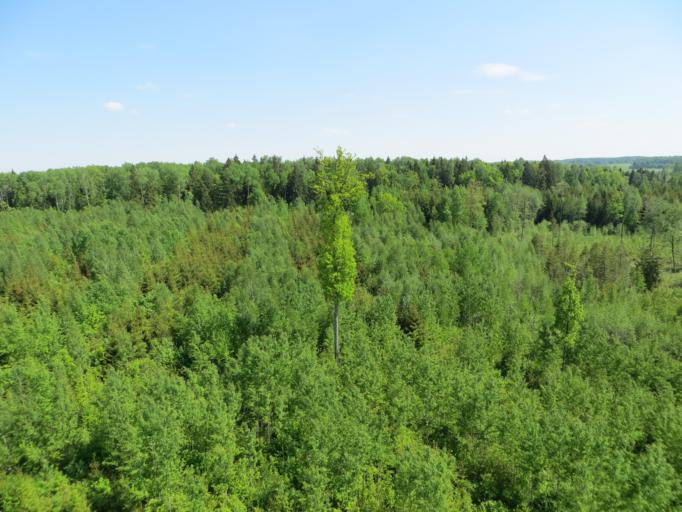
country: LT
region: Utenos apskritis
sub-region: Utena
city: Utena
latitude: 55.4502
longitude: 25.5712
